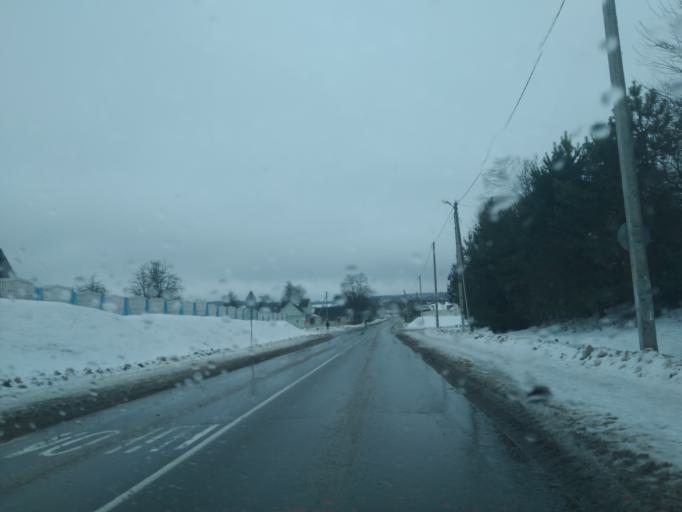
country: BY
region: Minsk
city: Stowbtsy
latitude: 53.5804
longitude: 26.8310
